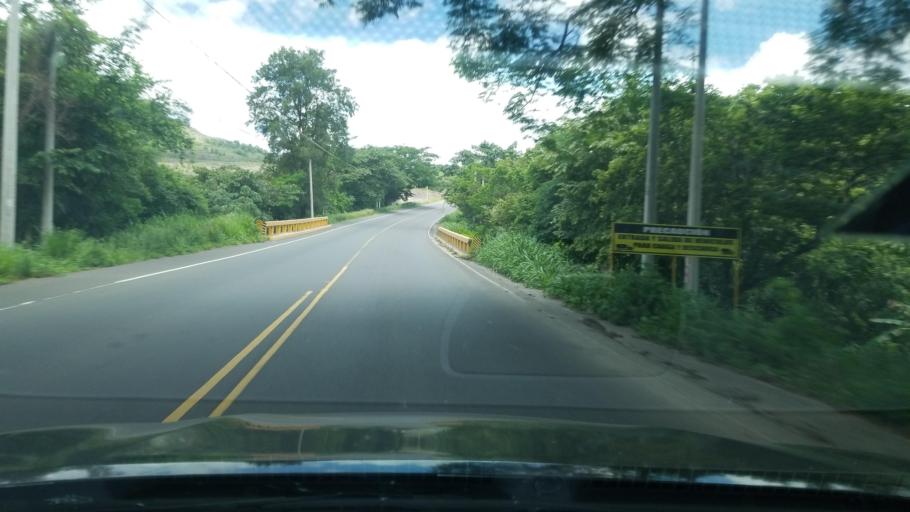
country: HN
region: Francisco Morazan
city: Cofradia
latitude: 14.3092
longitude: -87.2180
